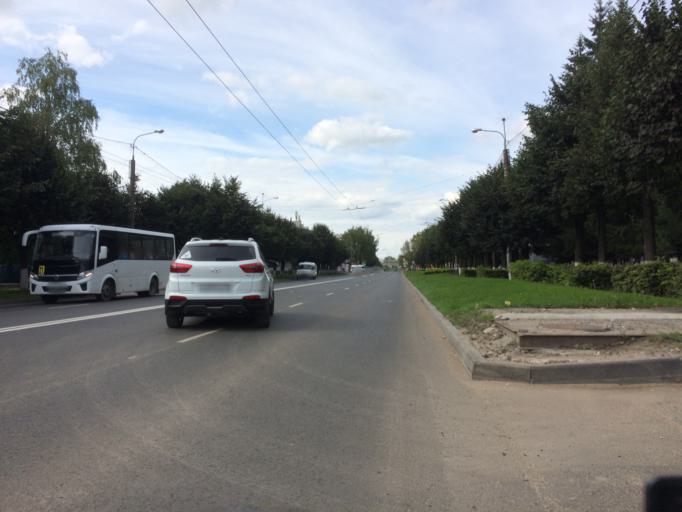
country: RU
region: Mariy-El
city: Yoshkar-Ola
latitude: 56.6353
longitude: 47.8759
